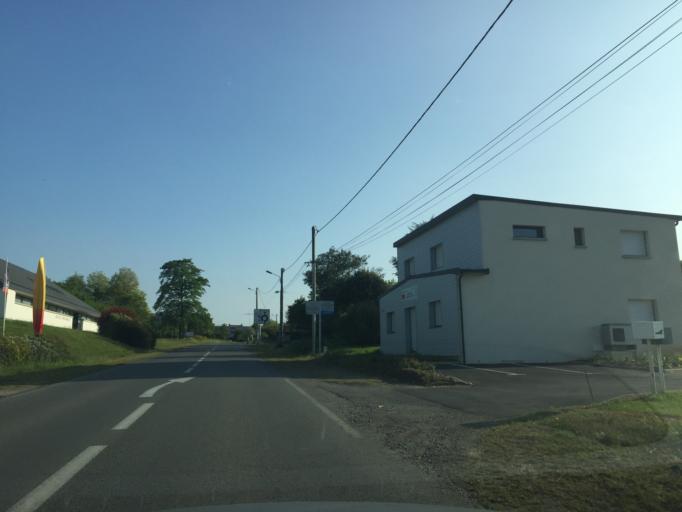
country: FR
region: Brittany
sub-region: Departement des Cotes-d'Armor
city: Matignon
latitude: 48.6017
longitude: -2.2862
